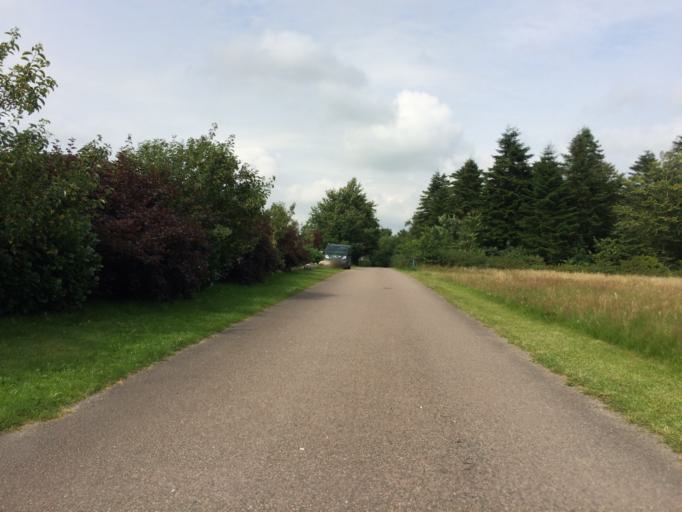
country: DK
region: Central Jutland
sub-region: Holstebro Kommune
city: Ulfborg
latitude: 56.2684
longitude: 8.3143
